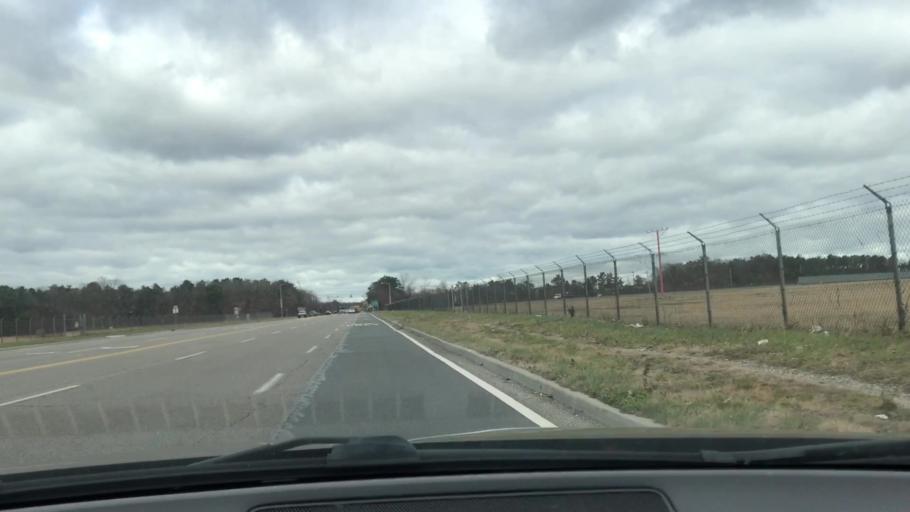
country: US
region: New York
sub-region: Suffolk County
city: Bohemia
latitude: 40.7864
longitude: -73.1145
